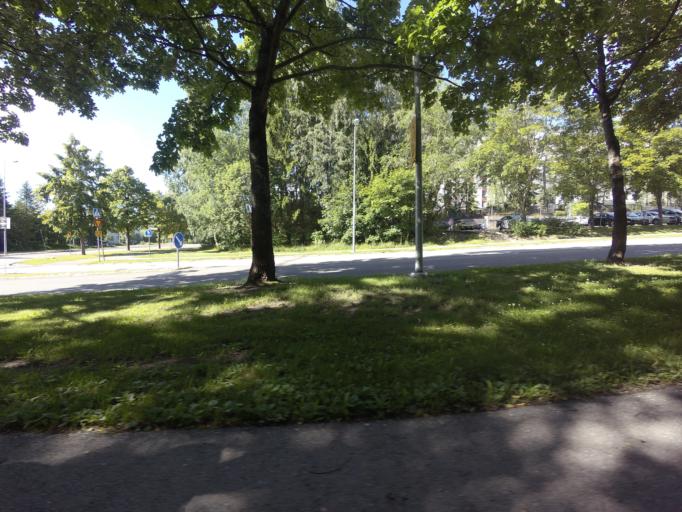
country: FI
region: Uusimaa
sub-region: Helsinki
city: Espoo
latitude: 60.1493
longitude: 24.6430
